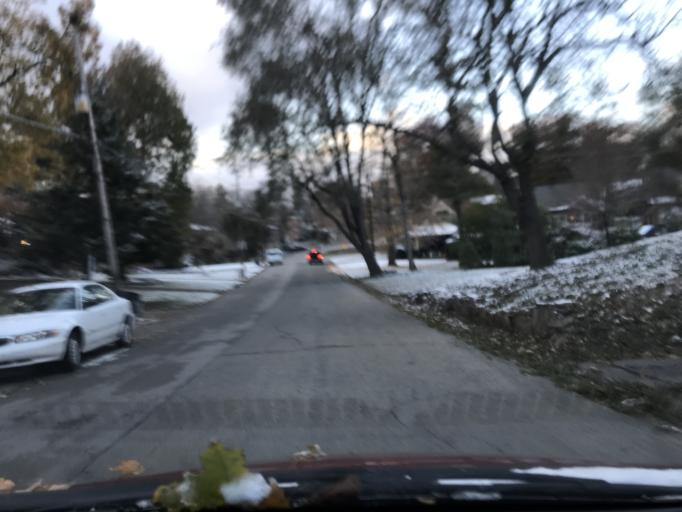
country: US
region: Kentucky
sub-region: Jefferson County
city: Indian Hills
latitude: 38.2581
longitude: -85.6969
